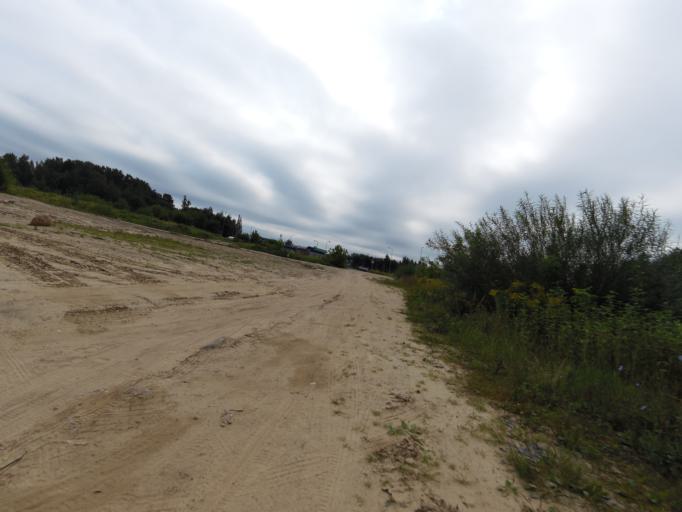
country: LT
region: Vilnius County
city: Rasos
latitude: 54.6576
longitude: 25.2906
